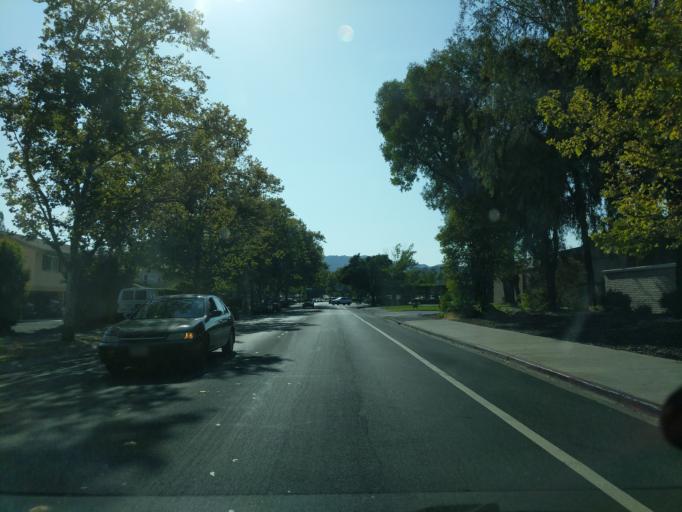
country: US
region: California
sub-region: Contra Costa County
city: Waldon
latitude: 37.9337
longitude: -122.0713
